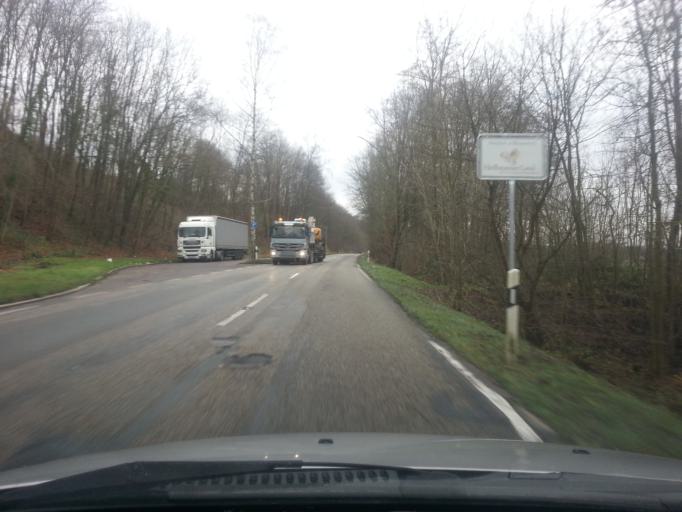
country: DE
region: Baden-Wuerttemberg
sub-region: Regierungsbezirk Stuttgart
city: Ittlingen
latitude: 49.2093
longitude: 8.9315
